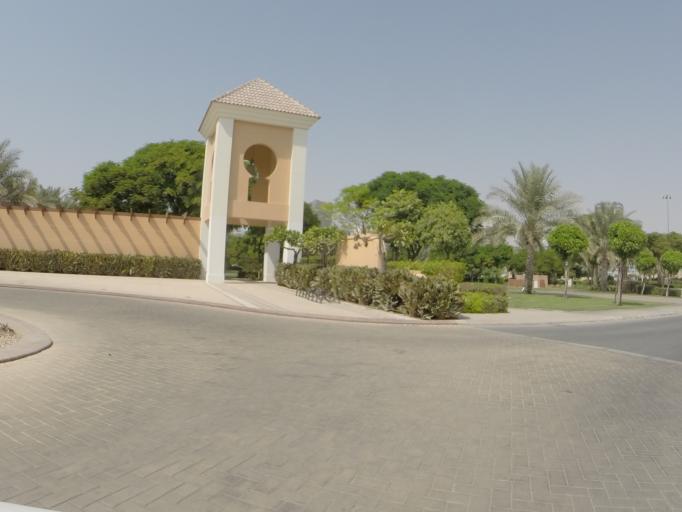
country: AE
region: Dubai
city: Dubai
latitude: 25.0317
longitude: 55.2188
